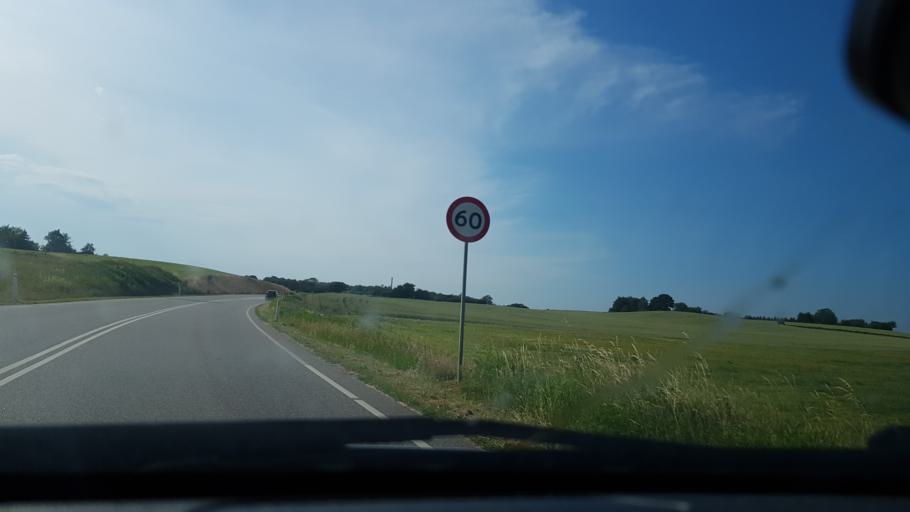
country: DK
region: Zealand
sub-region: Odsherred Kommune
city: Hojby
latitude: 55.8500
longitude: 11.5966
